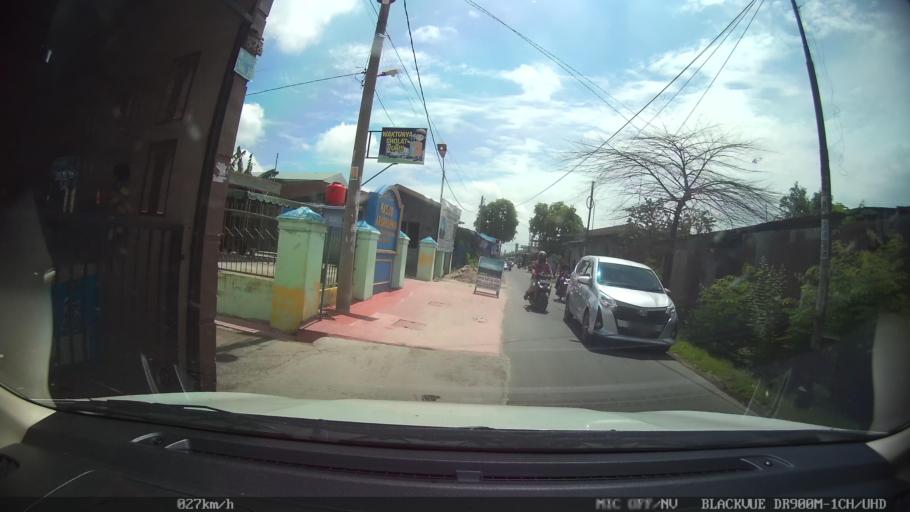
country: ID
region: North Sumatra
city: Medan
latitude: 3.6021
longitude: 98.7549
